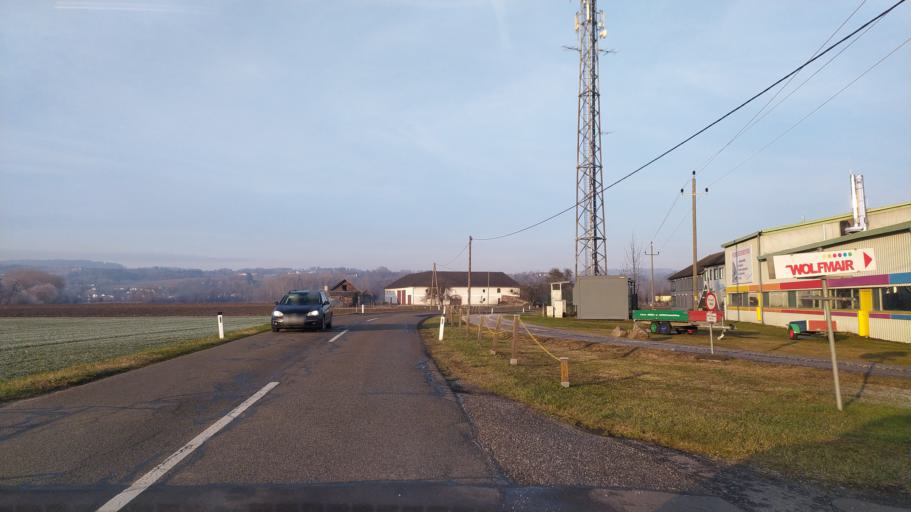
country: AT
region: Upper Austria
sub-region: Politischer Bezirk Urfahr-Umgebung
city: Goldworth
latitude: 48.3333
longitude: 14.1104
